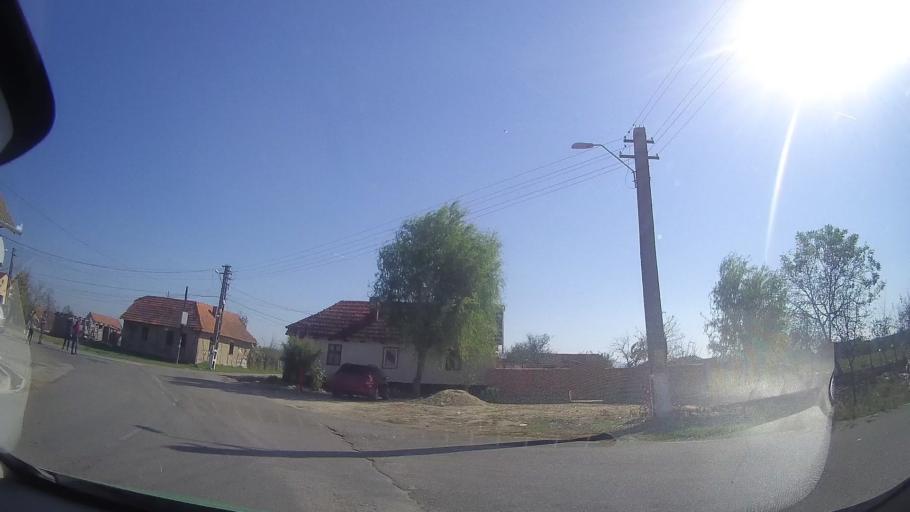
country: RO
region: Timis
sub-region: Comuna Traian Vuia
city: Traian Vuia
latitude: 45.7936
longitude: 22.0221
